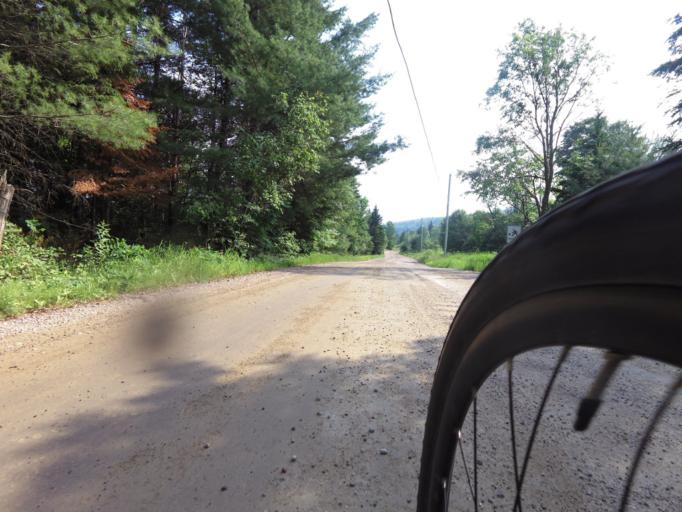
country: CA
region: Quebec
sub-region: Laurentides
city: Mont-Tremblant
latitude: 45.9426
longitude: -74.5963
